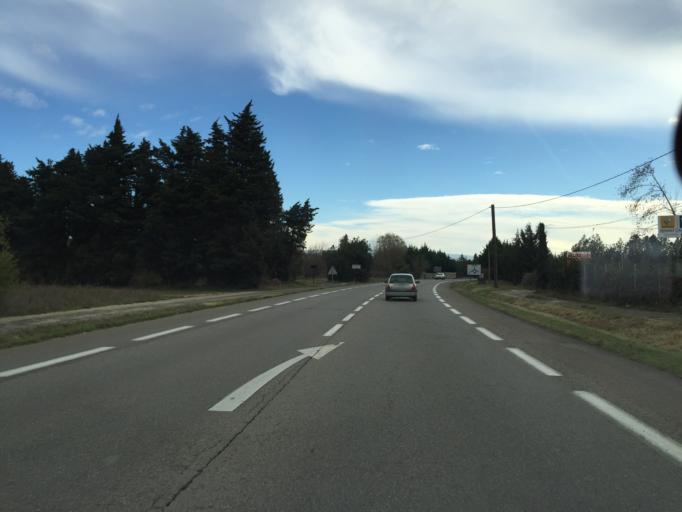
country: FR
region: Provence-Alpes-Cote d'Azur
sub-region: Departement du Vaucluse
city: L'Isle-sur-la-Sorgue
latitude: 43.9004
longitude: 5.0454
